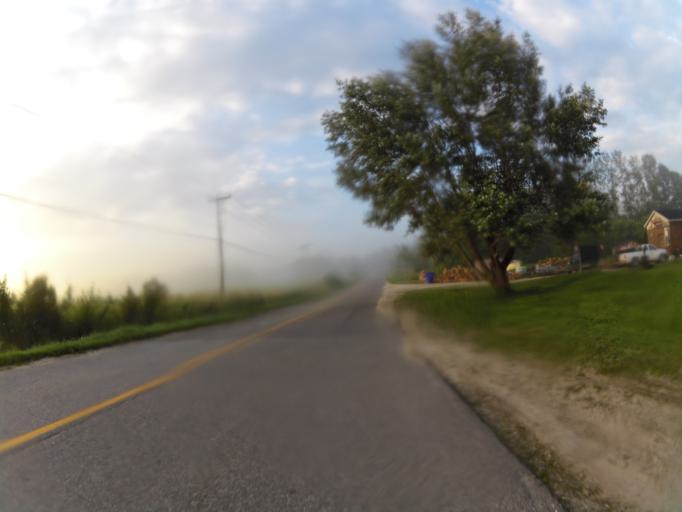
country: CA
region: Quebec
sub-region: Outaouais
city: Wakefield
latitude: 45.7084
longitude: -75.9603
